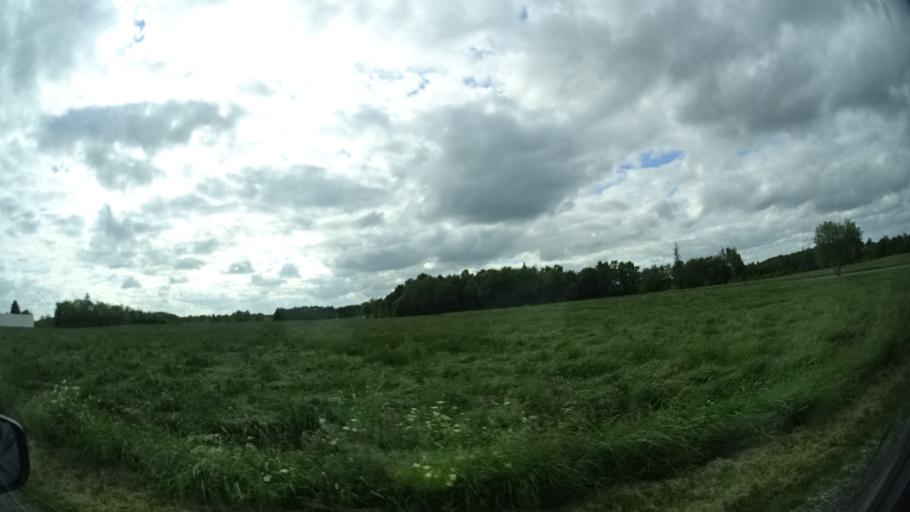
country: DK
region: Central Jutland
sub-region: Syddjurs Kommune
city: Ryomgard
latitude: 56.3896
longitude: 10.5125
